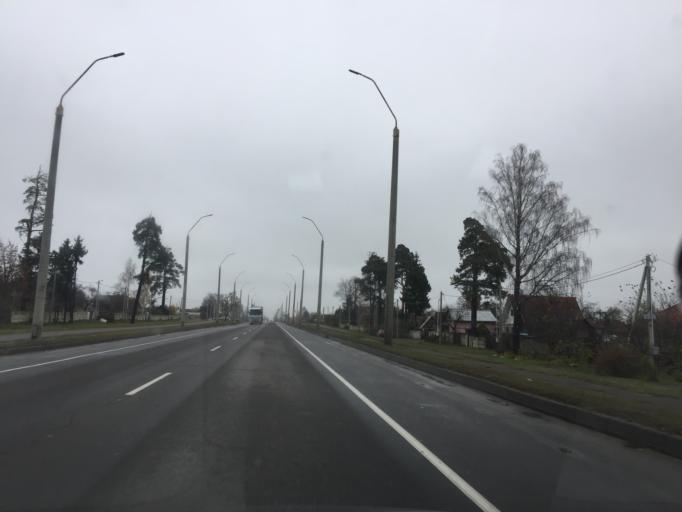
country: BY
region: Mogilev
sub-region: Mahilyowski Rayon
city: Veyno
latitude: 53.8449
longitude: 30.3596
